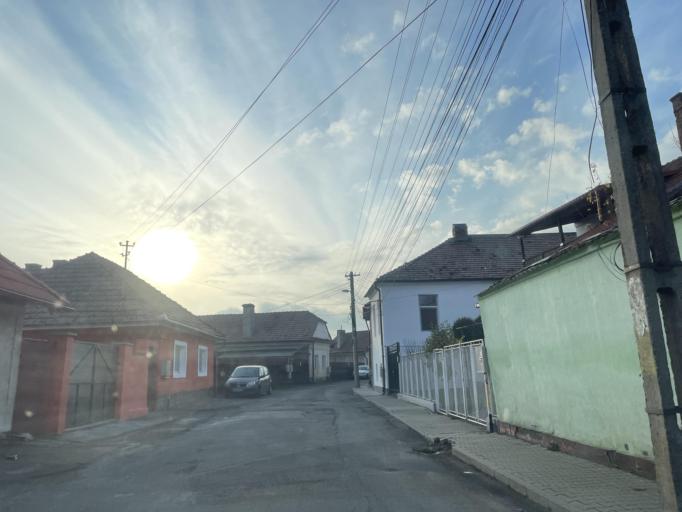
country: RO
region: Mures
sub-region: Municipiul Reghin
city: Reghin
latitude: 46.7768
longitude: 24.7012
